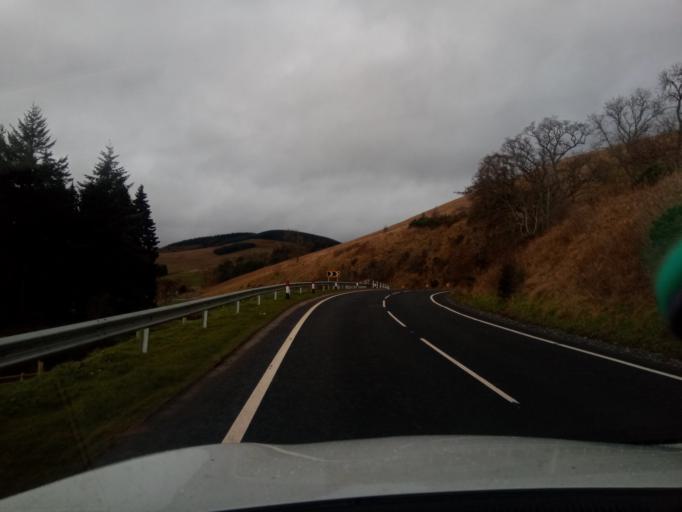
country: GB
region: Scotland
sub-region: The Scottish Borders
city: Innerleithen
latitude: 55.6416
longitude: -3.1008
